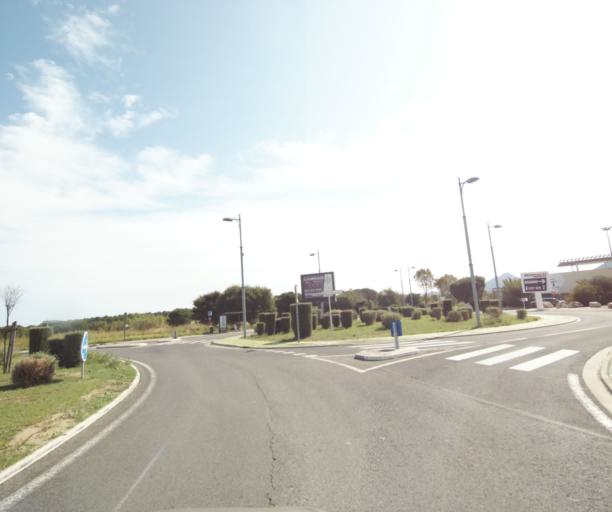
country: FR
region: Languedoc-Roussillon
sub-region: Departement des Pyrenees-Orientales
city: Argelers
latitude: 42.5599
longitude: 3.0090
